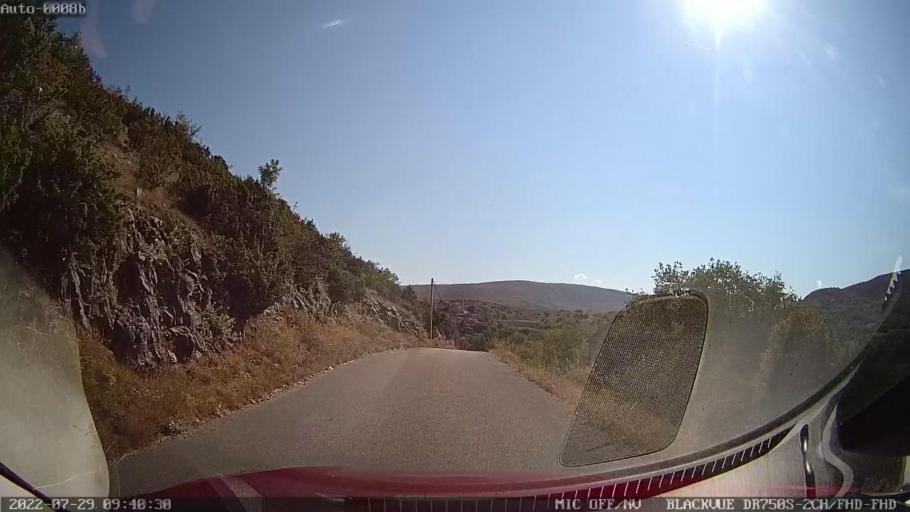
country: HR
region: Zadarska
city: Obrovac
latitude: 44.1949
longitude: 15.7645
